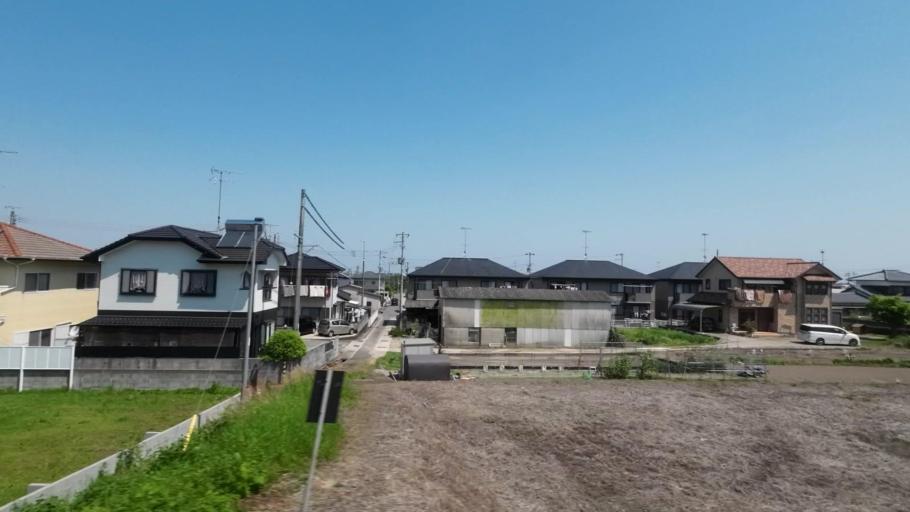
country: JP
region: Ehime
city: Saijo
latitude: 33.8979
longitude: 133.1115
